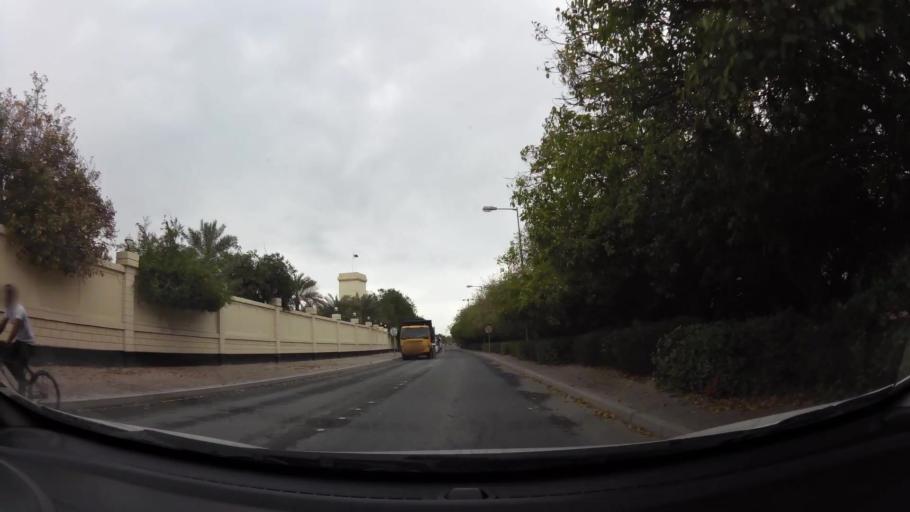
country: BH
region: Central Governorate
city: Madinat Hamad
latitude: 26.1564
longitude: 50.4528
